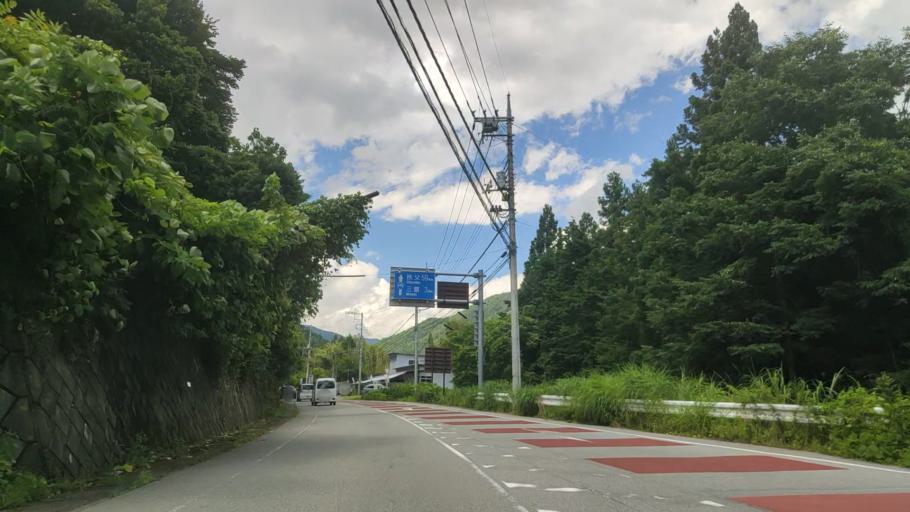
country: JP
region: Yamanashi
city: Enzan
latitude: 35.7664
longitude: 138.7364
